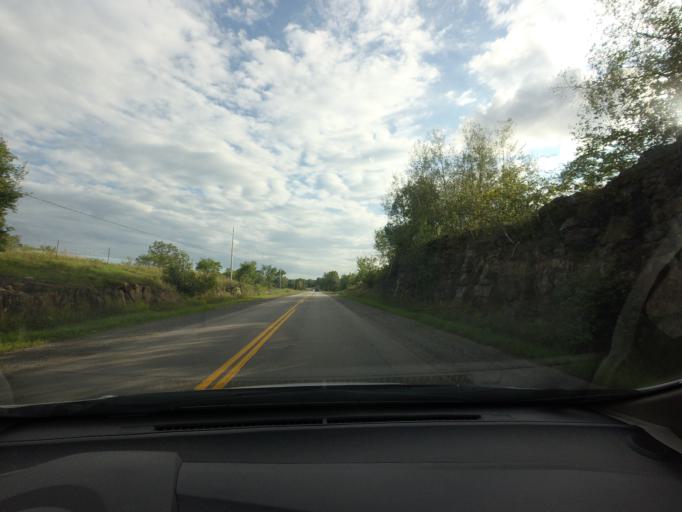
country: CA
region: Ontario
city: Perth
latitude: 44.7358
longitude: -76.3941
